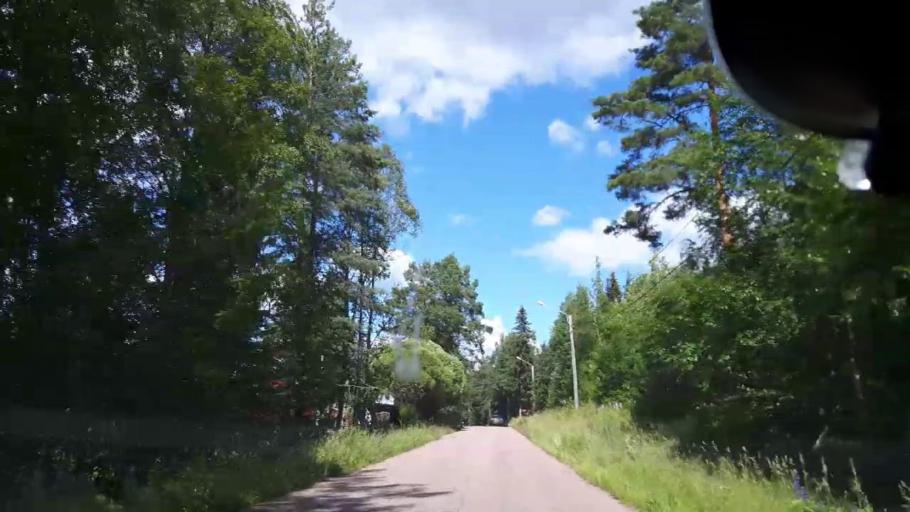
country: SE
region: Jaemtland
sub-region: Ragunda Kommun
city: Hammarstrand
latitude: 62.9501
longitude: 16.6877
